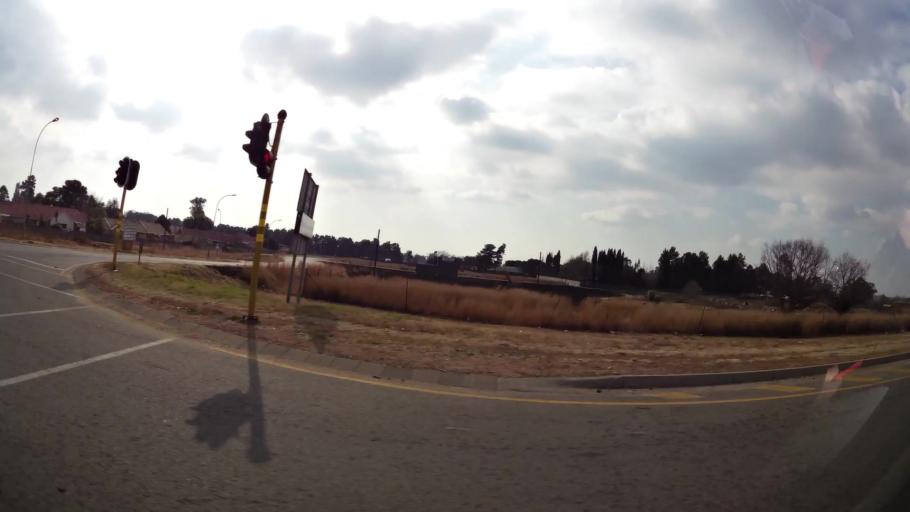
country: ZA
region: Gauteng
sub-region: Ekurhuleni Metropolitan Municipality
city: Benoni
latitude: -26.1271
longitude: 28.2633
